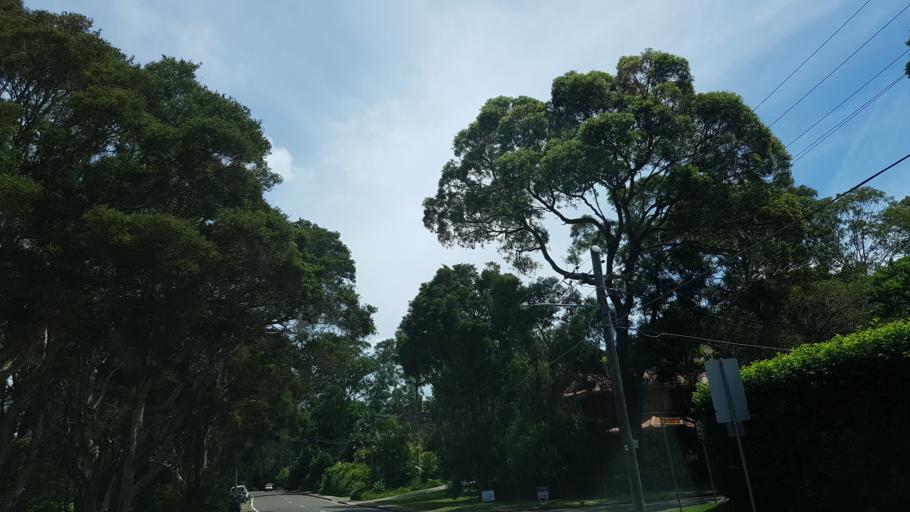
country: AU
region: New South Wales
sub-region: Pittwater
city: Bay View
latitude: -33.6666
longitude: 151.3003
